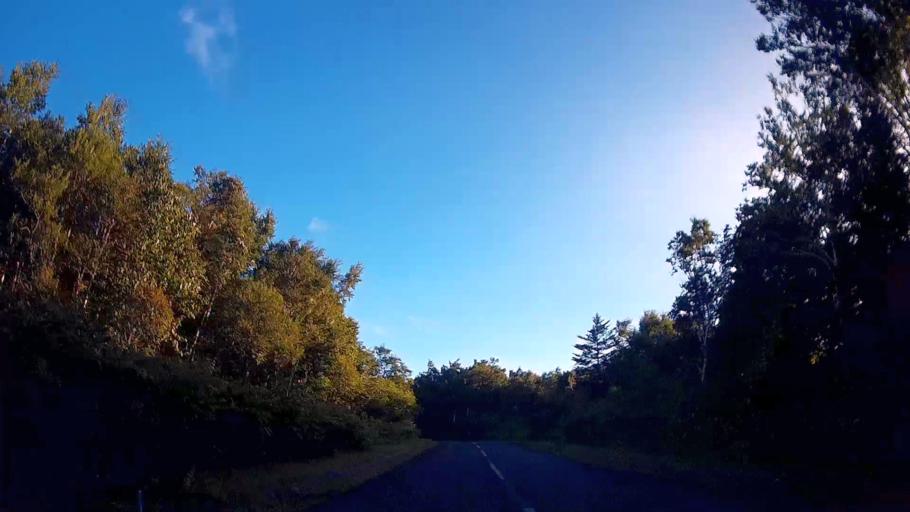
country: JP
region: Hokkaido
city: Iwanai
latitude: 42.6361
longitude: 140.0322
